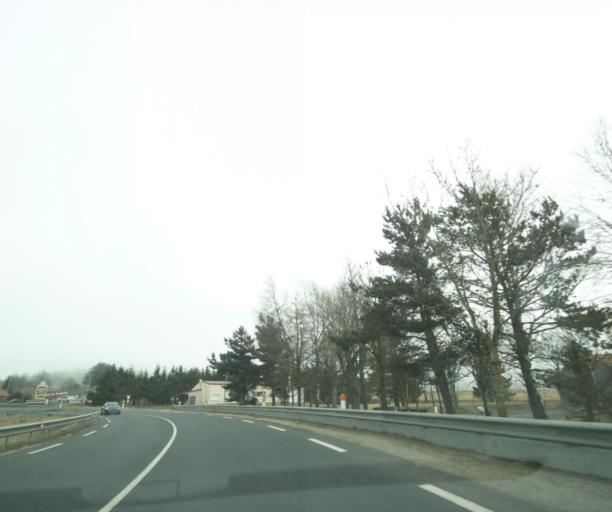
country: FR
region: Languedoc-Roussillon
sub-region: Departement de la Lozere
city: Langogne
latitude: 44.7747
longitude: 3.8865
